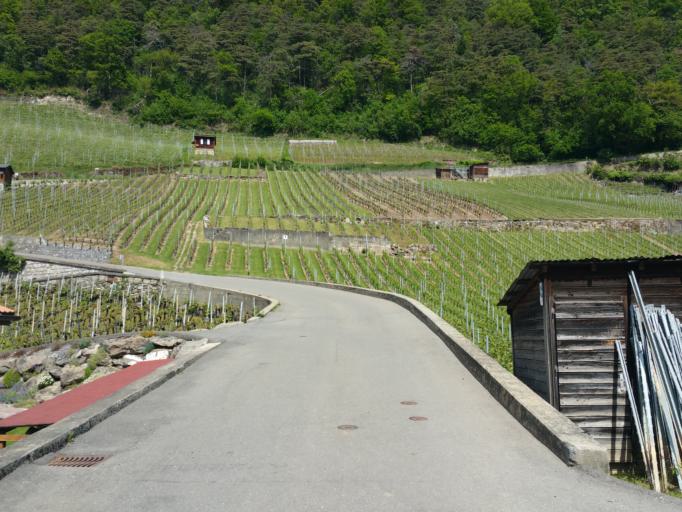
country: CH
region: Vaud
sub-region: Aigle District
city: Bex
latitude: 46.2547
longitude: 7.0189
